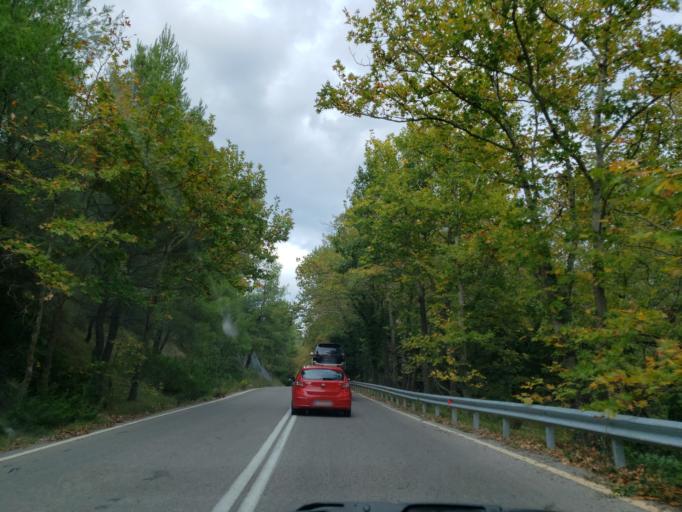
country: GR
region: Attica
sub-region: Nomarchia Anatolikis Attikis
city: Varnavas
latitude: 38.2109
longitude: 23.9064
